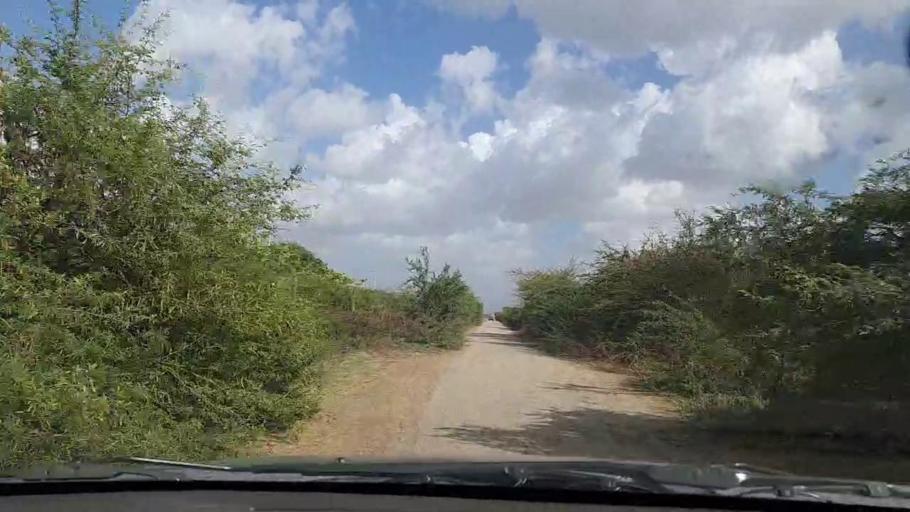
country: PK
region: Sindh
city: Keti Bandar
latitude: 24.0972
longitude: 67.6056
